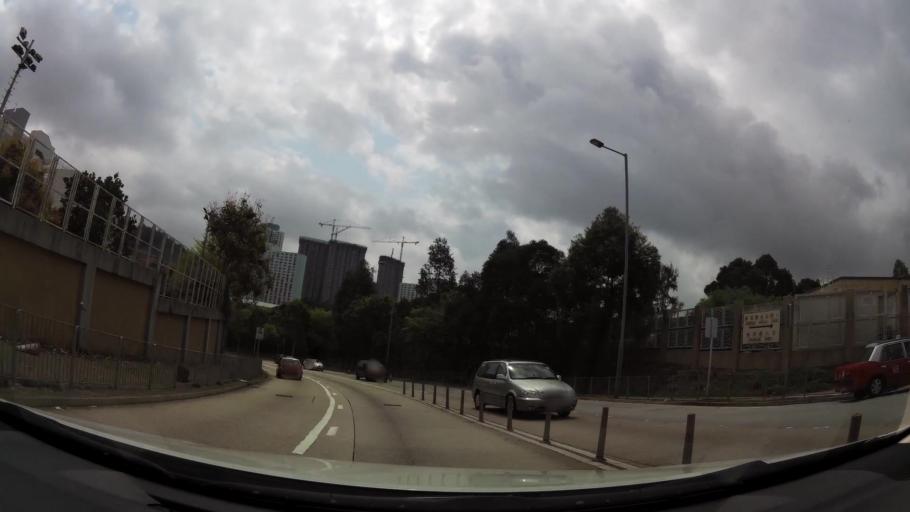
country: HK
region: Kowloon City
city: Kowloon
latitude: 22.3301
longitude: 114.2225
